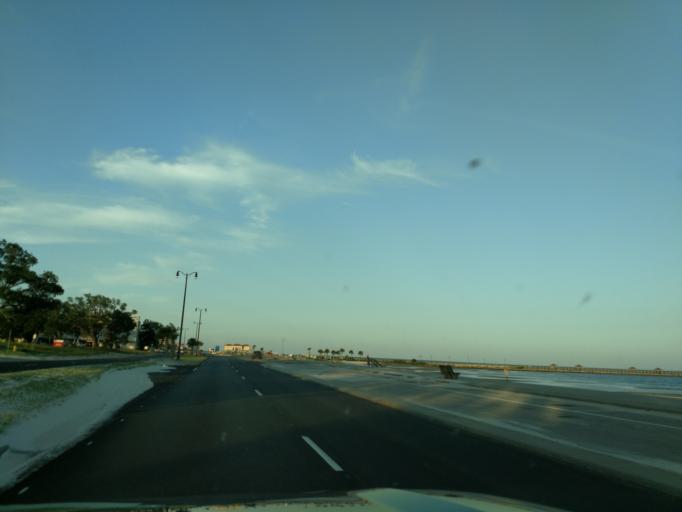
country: US
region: Mississippi
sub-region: Harrison County
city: Gulfport
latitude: 30.3775
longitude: -89.0485
